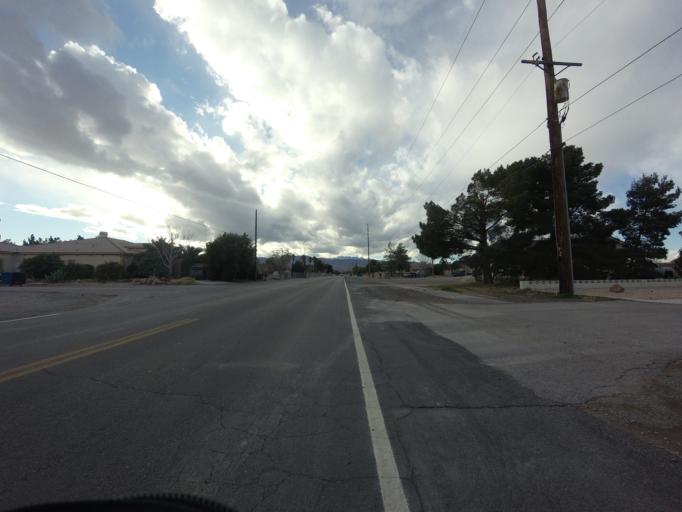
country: US
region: Nevada
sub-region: Clark County
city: Las Vegas
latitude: 36.2688
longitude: -115.2315
